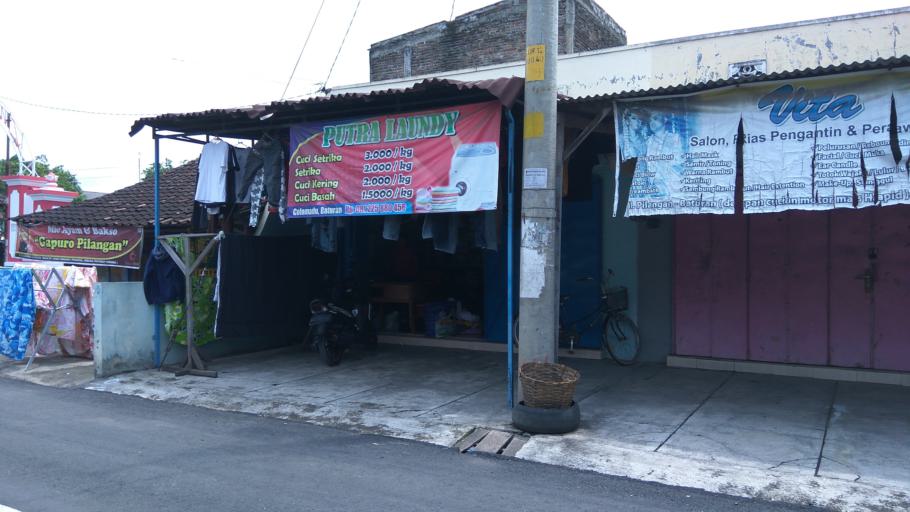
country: ID
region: Central Java
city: Colomadu
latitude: -7.5408
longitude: 110.7913
